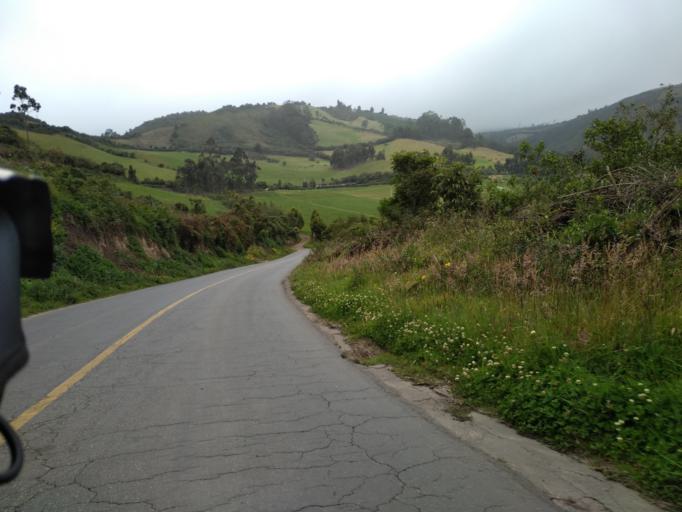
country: EC
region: Carchi
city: El Angel
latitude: 0.6327
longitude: -77.9315
